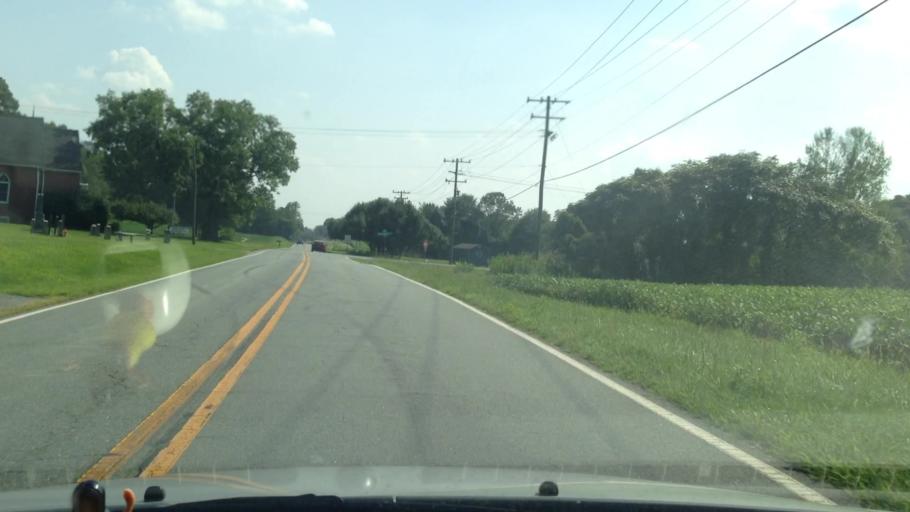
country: US
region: North Carolina
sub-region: Guilford County
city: Oak Ridge
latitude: 36.2037
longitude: -80.0580
